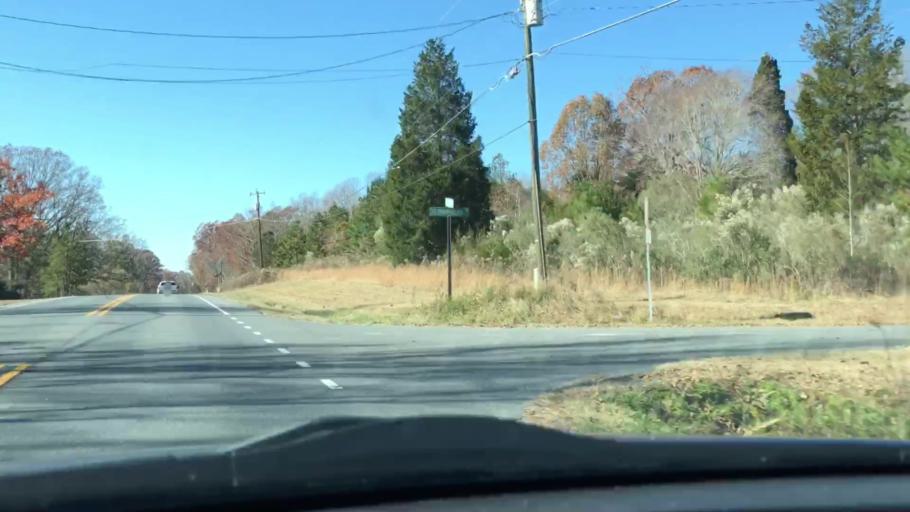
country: US
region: North Carolina
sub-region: Randolph County
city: Asheboro
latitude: 35.6766
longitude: -79.8799
